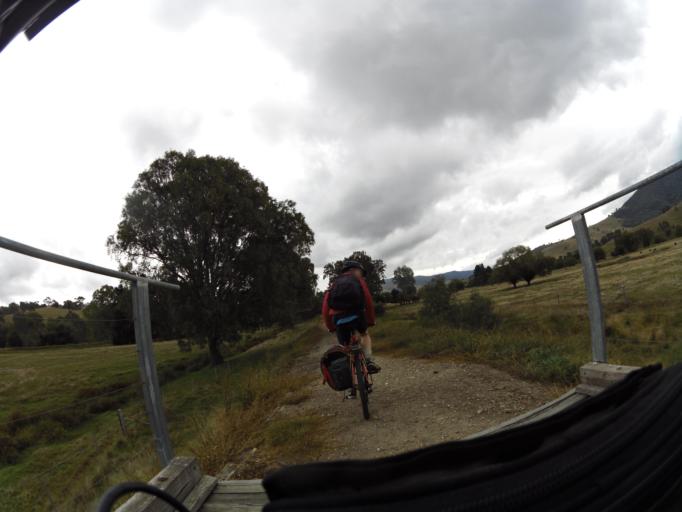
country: AU
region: New South Wales
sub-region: Albury Municipality
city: East Albury
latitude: -36.1938
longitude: 147.3177
